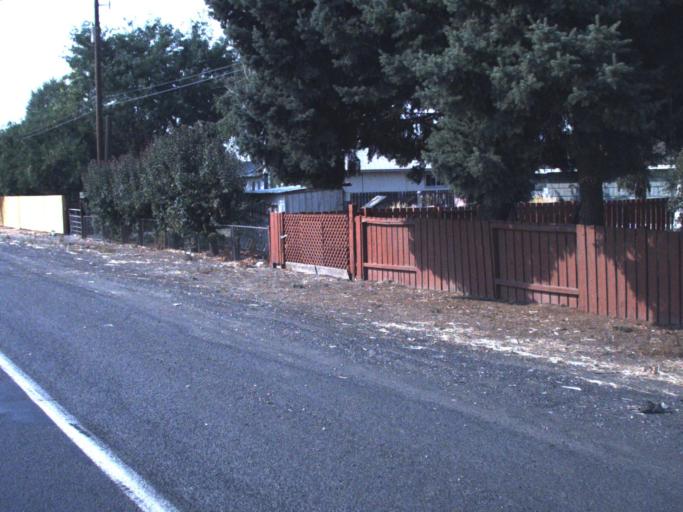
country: US
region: Washington
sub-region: Yakima County
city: Toppenish
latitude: 46.3691
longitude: -120.3176
